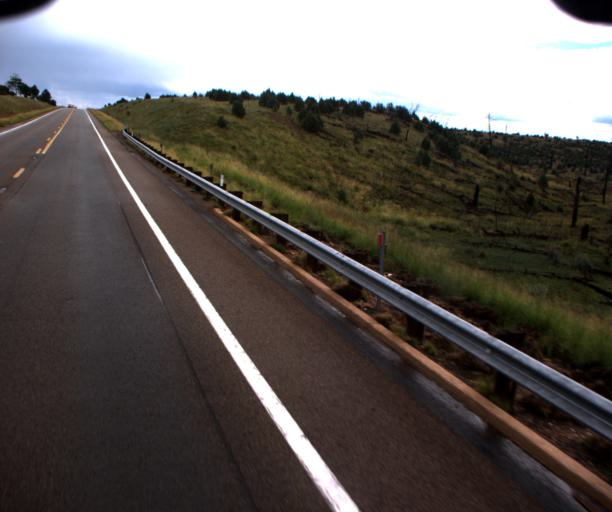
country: US
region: Arizona
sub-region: Navajo County
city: Heber-Overgaard
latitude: 34.3811
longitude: -110.4811
